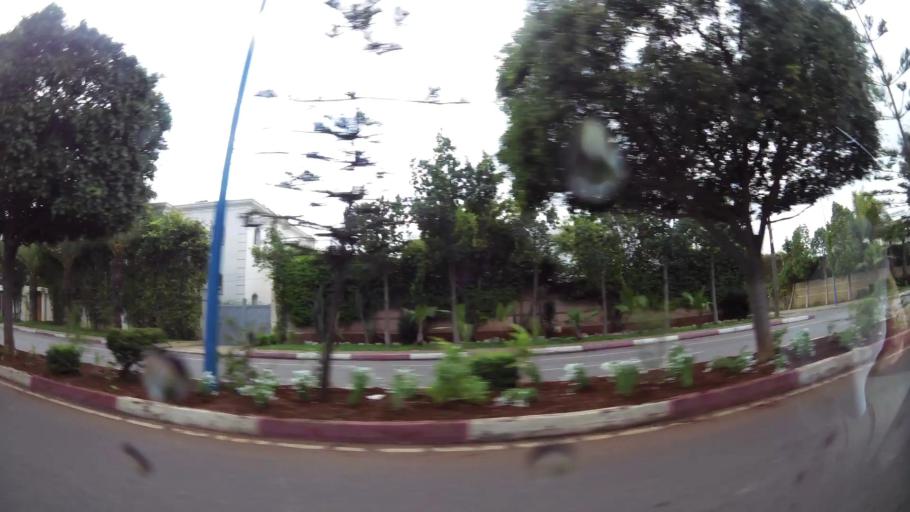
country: MA
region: Grand Casablanca
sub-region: Casablanca
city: Casablanca
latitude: 33.5441
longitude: -7.6312
